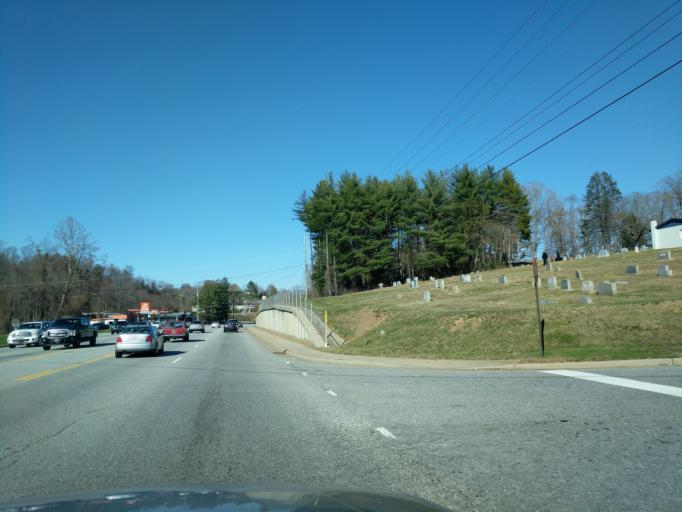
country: US
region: North Carolina
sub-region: Buncombe County
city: Biltmore Forest
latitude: 35.5434
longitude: -82.5214
